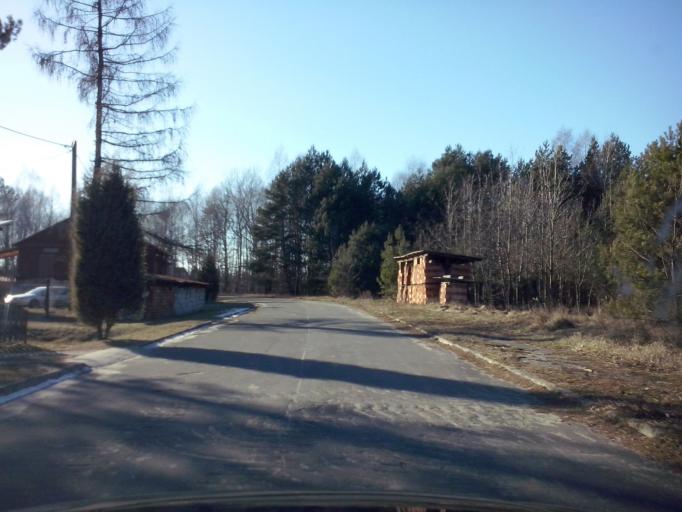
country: PL
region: Subcarpathian Voivodeship
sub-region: Powiat nizanski
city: Harasiuki
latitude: 50.5298
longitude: 22.4533
